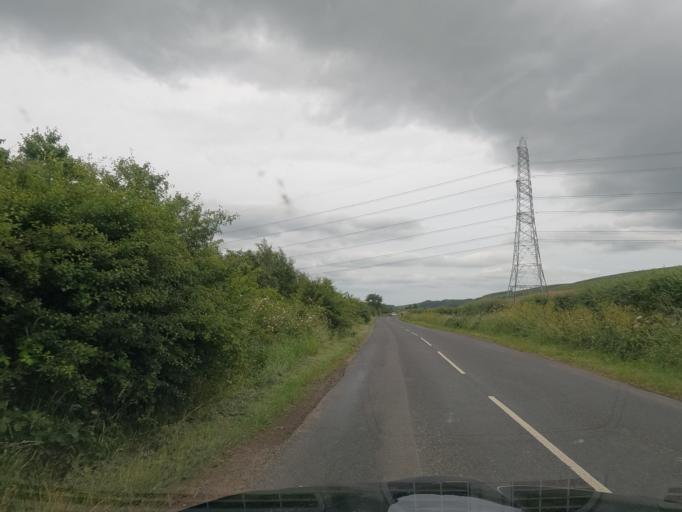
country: GB
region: England
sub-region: Northumberland
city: Wooler
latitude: 55.5493
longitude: -2.0050
